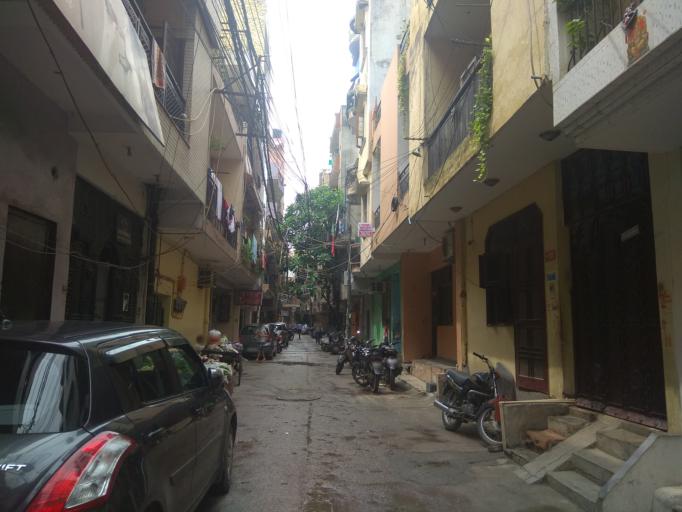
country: IN
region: NCT
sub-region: New Delhi
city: New Delhi
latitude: 28.5740
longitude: 77.2562
